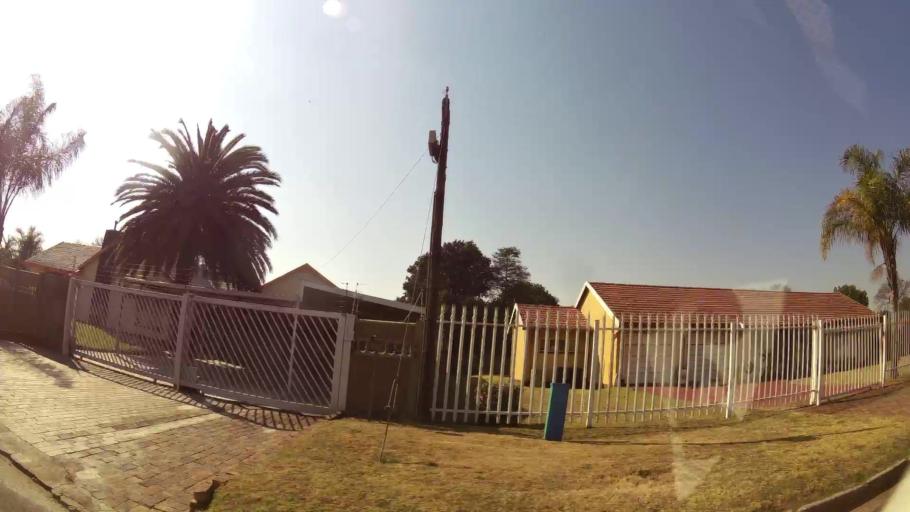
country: ZA
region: Gauteng
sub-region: Ekurhuleni Metropolitan Municipality
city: Boksburg
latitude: -26.2486
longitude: 28.2658
